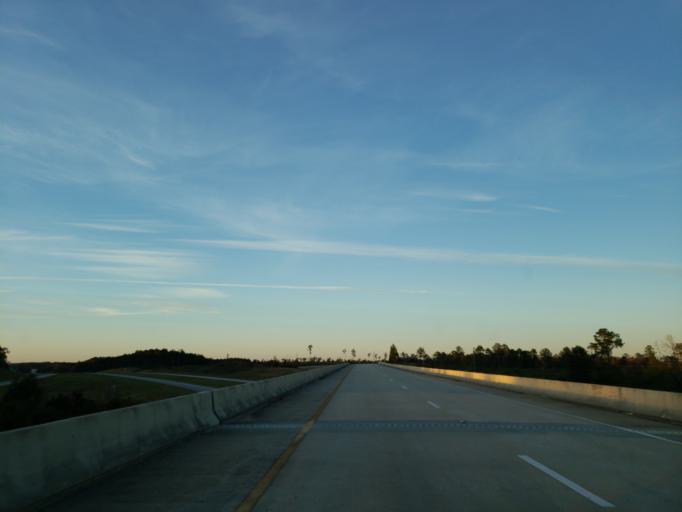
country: US
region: Mississippi
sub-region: Wayne County
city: Belmont
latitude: 31.4528
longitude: -88.4646
